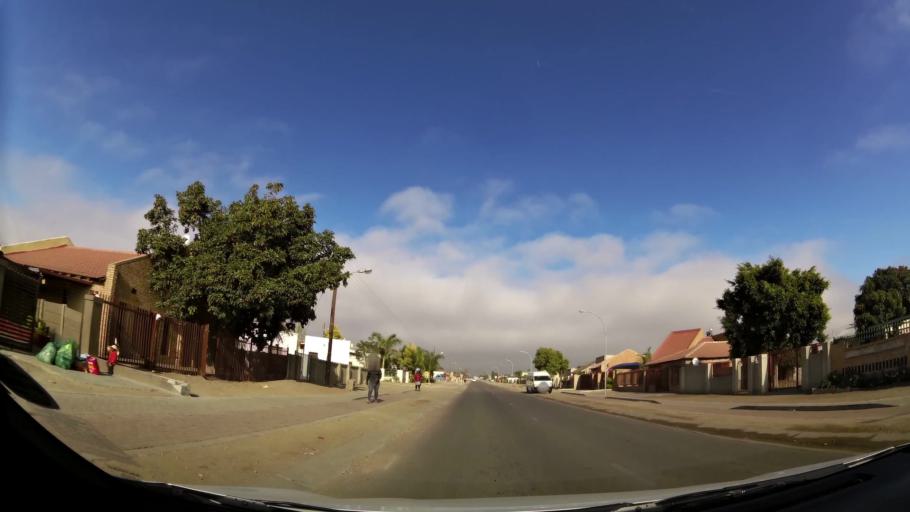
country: ZA
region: Limpopo
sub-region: Capricorn District Municipality
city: Polokwane
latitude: -23.8446
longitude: 29.3891
